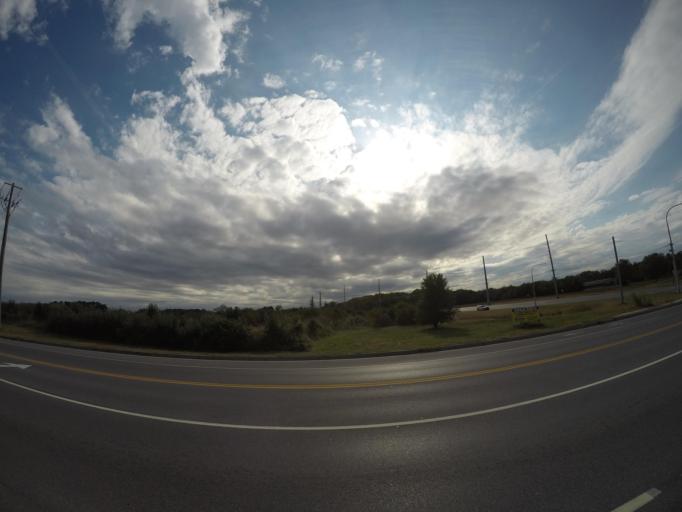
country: US
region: Delaware
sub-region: Sussex County
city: Lewes
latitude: 38.7325
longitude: -75.1531
